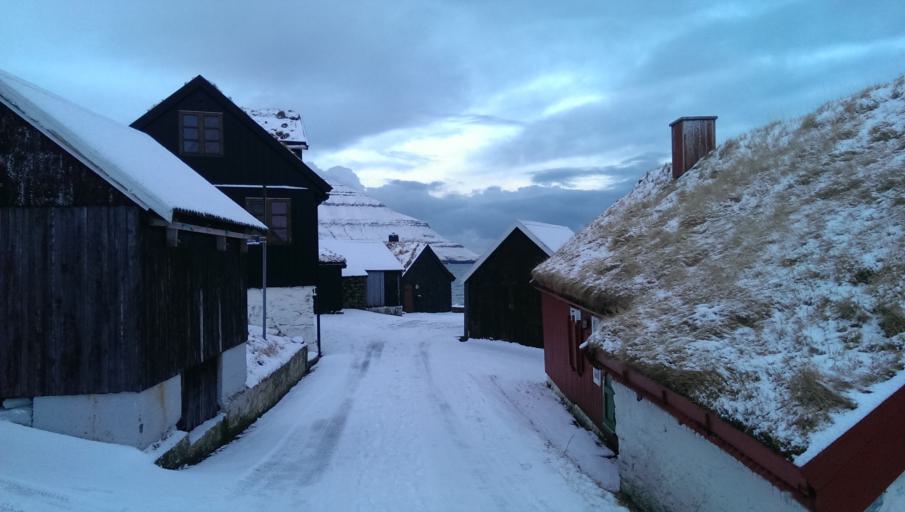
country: FO
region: Eysturoy
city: Fuglafjordur
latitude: 62.2827
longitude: -6.9134
